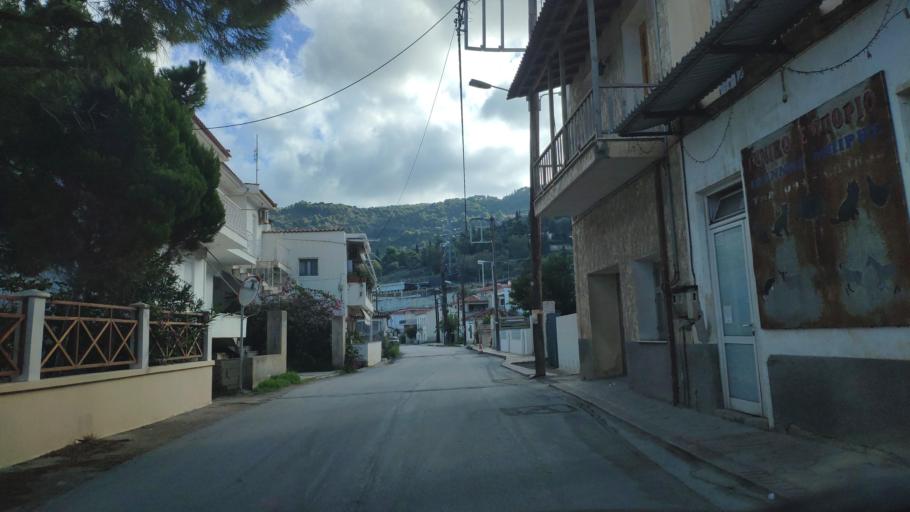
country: GR
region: West Greece
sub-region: Nomos Achaias
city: Aiyira
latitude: 38.1306
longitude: 22.4137
